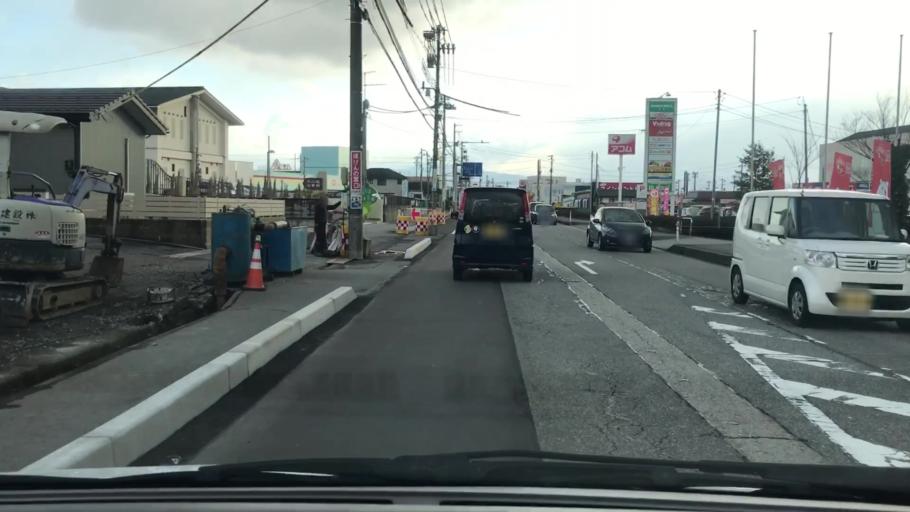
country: JP
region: Toyama
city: Toyama-shi
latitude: 36.6795
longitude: 137.2368
